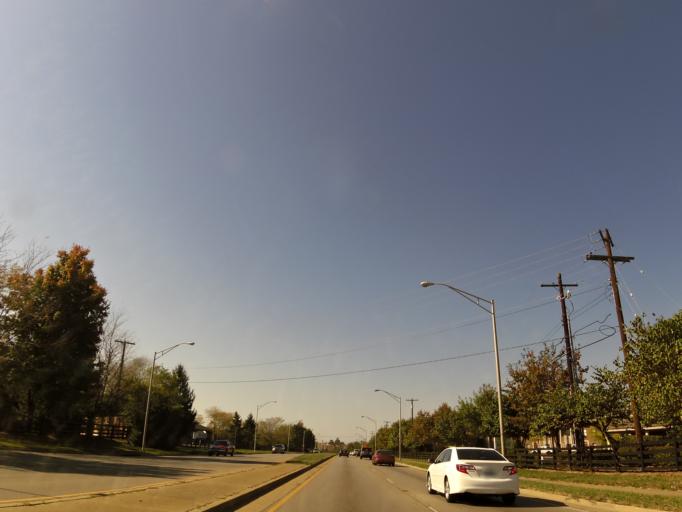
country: US
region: Kentucky
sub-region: Fayette County
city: Lexington
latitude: 38.0072
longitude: -84.4323
